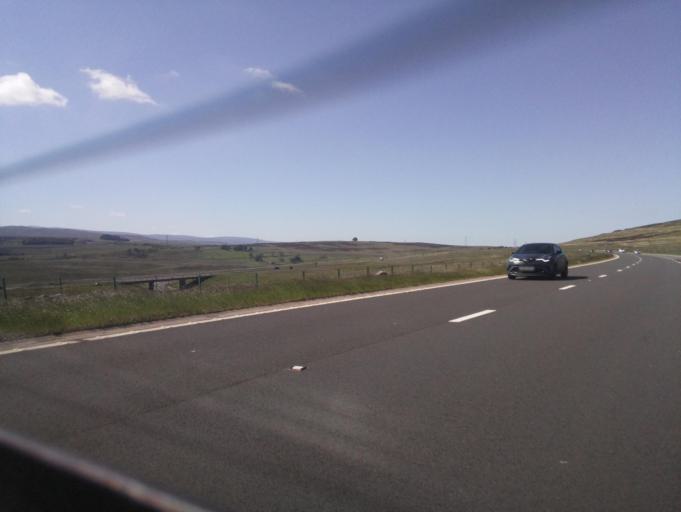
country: GB
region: England
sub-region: Cumbria
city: Appleby-in-Westmorland
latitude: 54.4834
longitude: -2.6335
